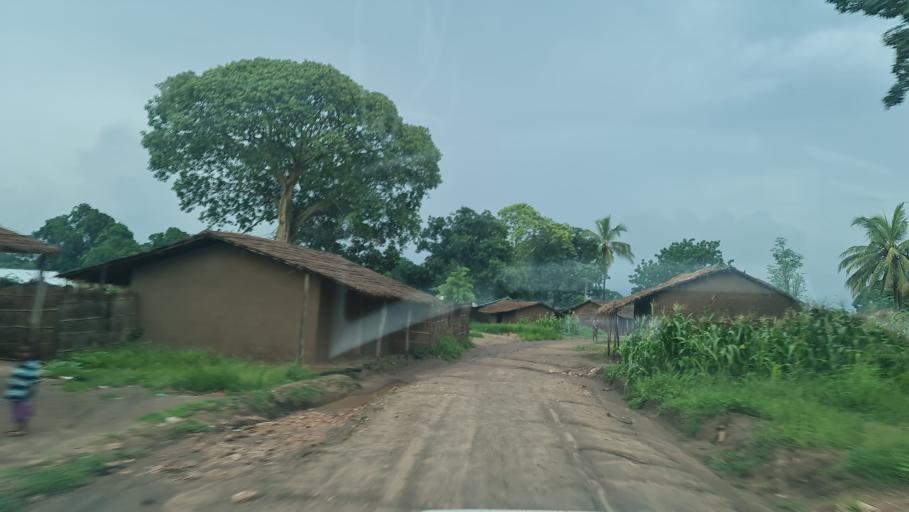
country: MZ
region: Nampula
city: Nacala
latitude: -13.9505
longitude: 40.2760
